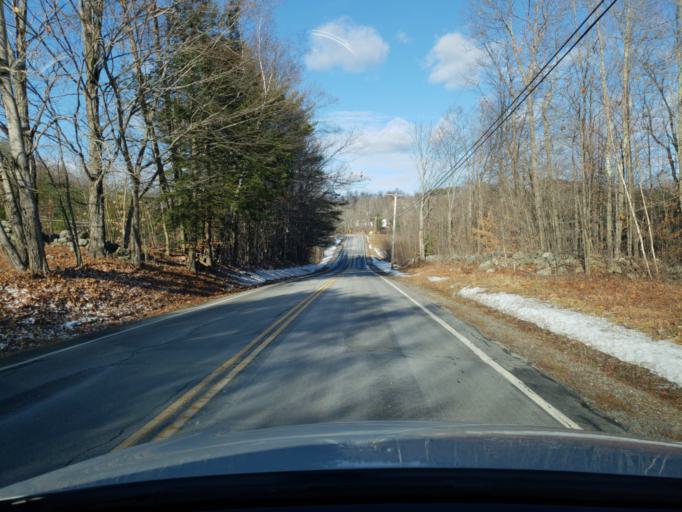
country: US
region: New Hampshire
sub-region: Hillsborough County
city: New Boston
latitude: 42.9885
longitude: -71.7014
